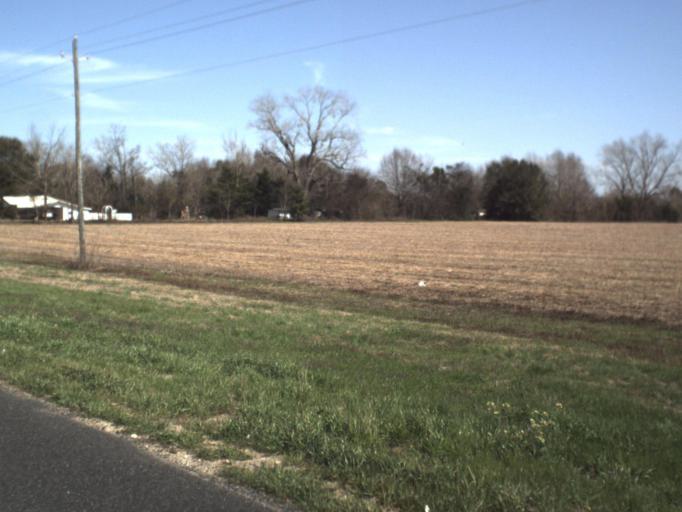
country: US
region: Florida
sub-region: Jackson County
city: Graceville
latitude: 30.9788
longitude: -85.4085
